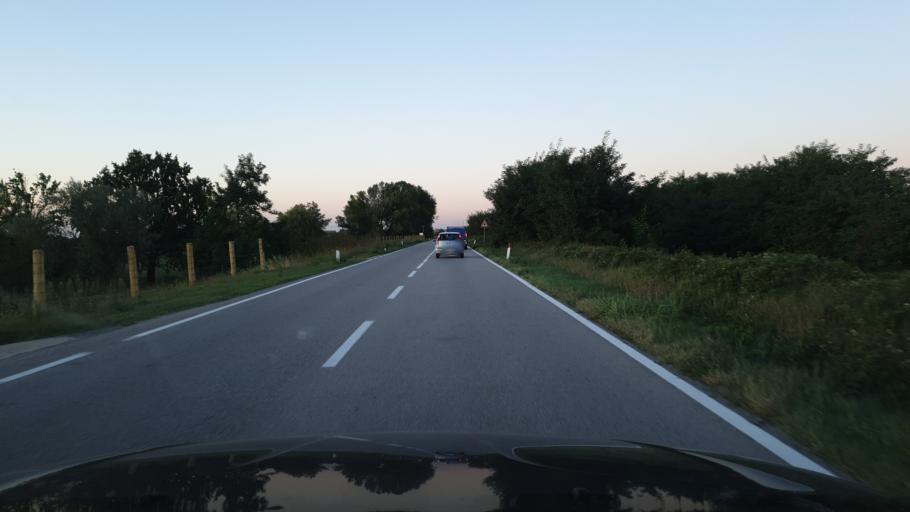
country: IT
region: Emilia-Romagna
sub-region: Provincia di Bologna
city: Ca De Fabbri
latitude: 44.6077
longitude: 11.4450
